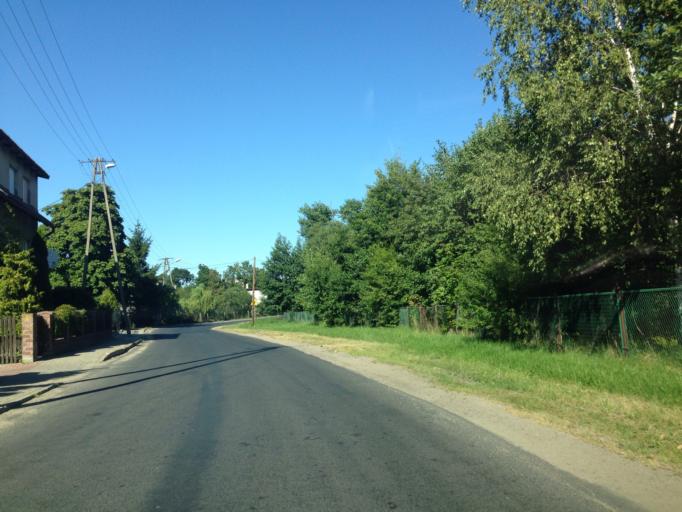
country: PL
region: Kujawsko-Pomorskie
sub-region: Powiat brodnicki
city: Brodnica
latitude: 53.2103
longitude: 19.4401
